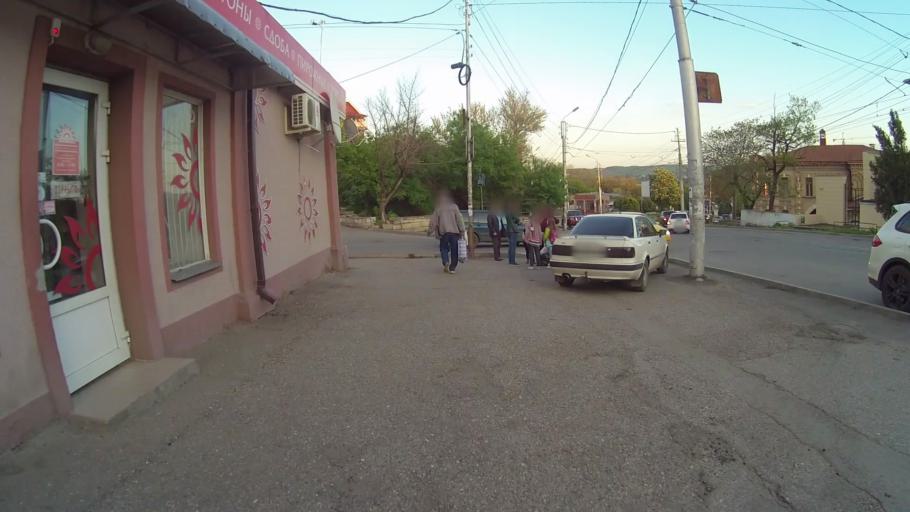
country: RU
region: Stavropol'skiy
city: Goryachevodskiy
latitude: 44.0352
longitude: 43.0789
